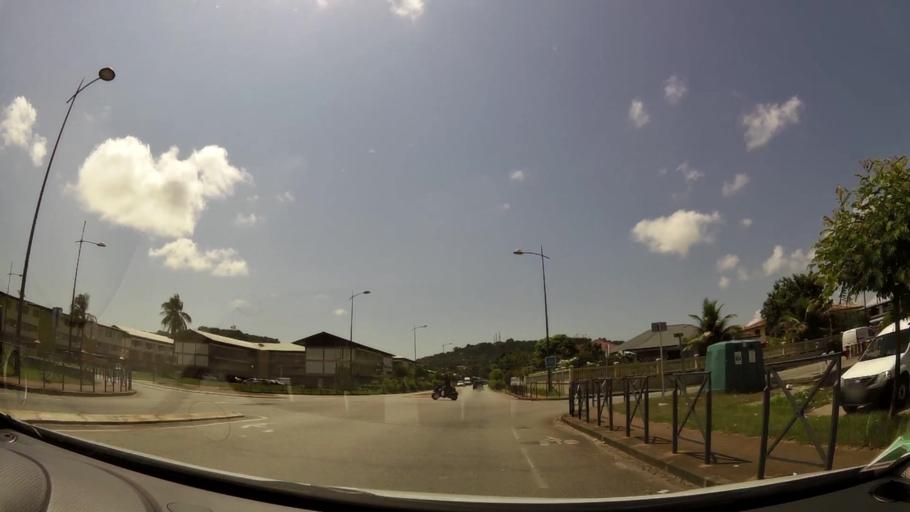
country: GF
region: Guyane
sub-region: Guyane
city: Cayenne
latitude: 4.9192
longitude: -52.3179
